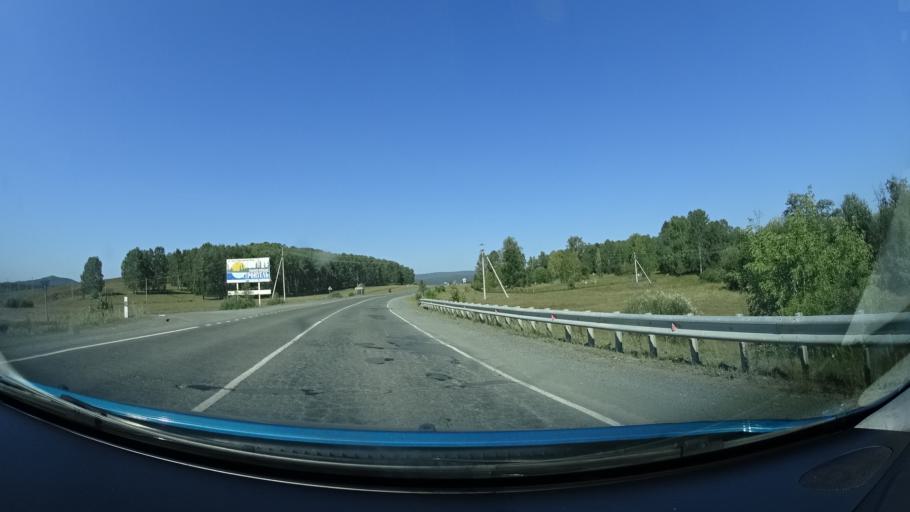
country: RU
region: Bashkortostan
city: Abzakovo
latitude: 53.8231
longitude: 58.6152
